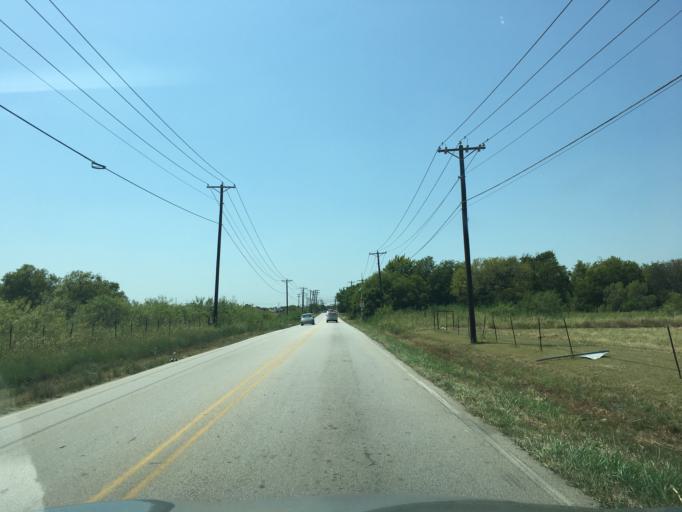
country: US
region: Texas
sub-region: Tarrant County
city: Crowley
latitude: 32.6142
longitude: -97.3449
